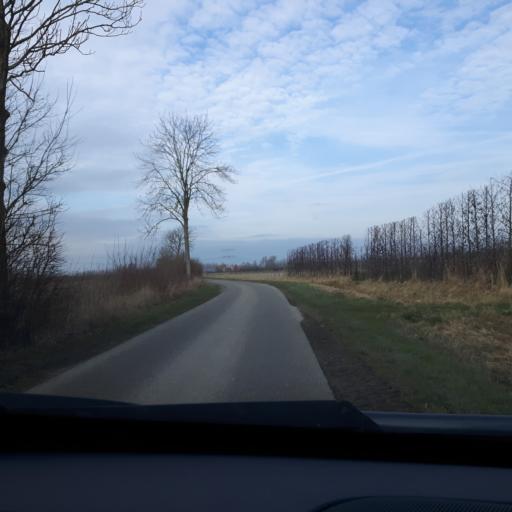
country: NL
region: Zeeland
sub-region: Gemeente Goes
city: Goes
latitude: 51.4333
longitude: 3.9159
